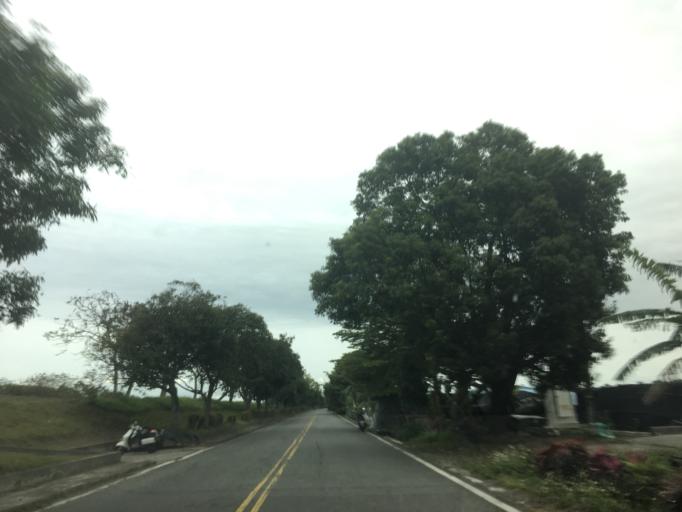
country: TW
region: Taiwan
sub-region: Taitung
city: Taitung
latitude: 22.8005
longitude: 121.1357
